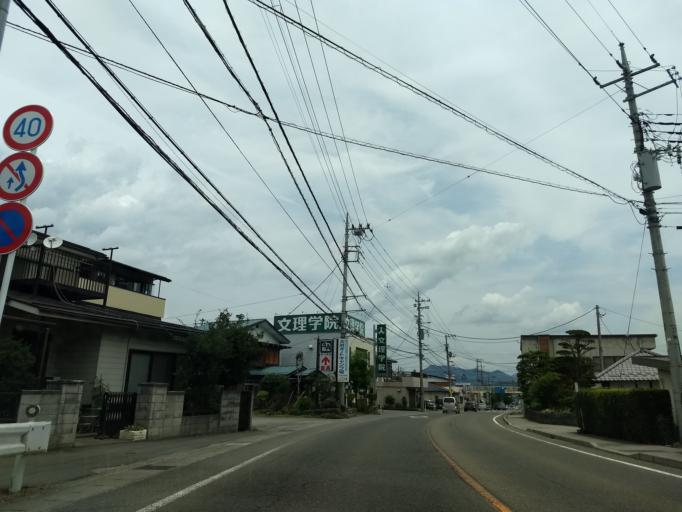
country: JP
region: Yamanashi
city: Otsuki
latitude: 35.5354
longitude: 138.8700
